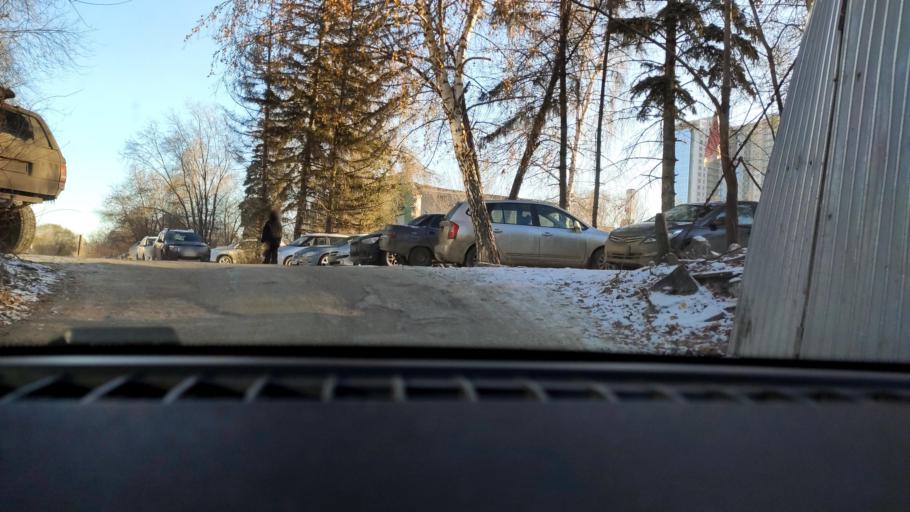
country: RU
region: Samara
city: Samara
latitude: 53.2165
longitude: 50.1402
